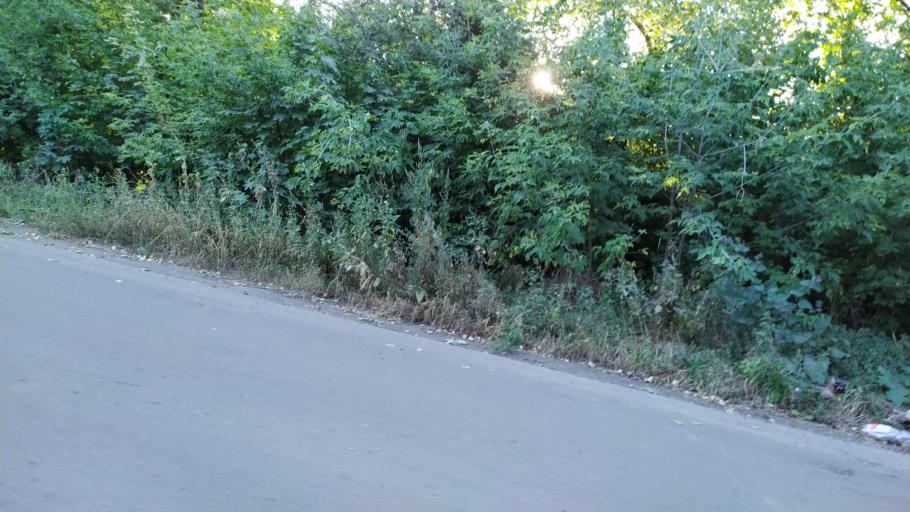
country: RU
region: Kursk
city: Kursk
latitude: 51.6537
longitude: 36.1320
